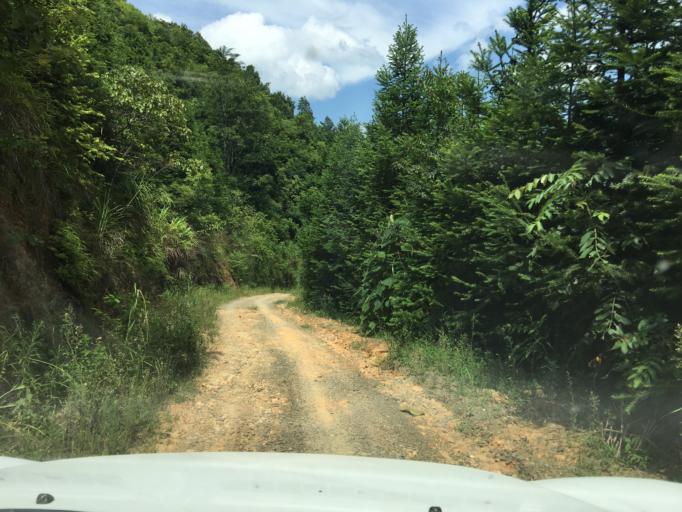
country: CN
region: Guangxi Zhuangzu Zizhiqu
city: Tongle
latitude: 24.9712
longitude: 105.9722
